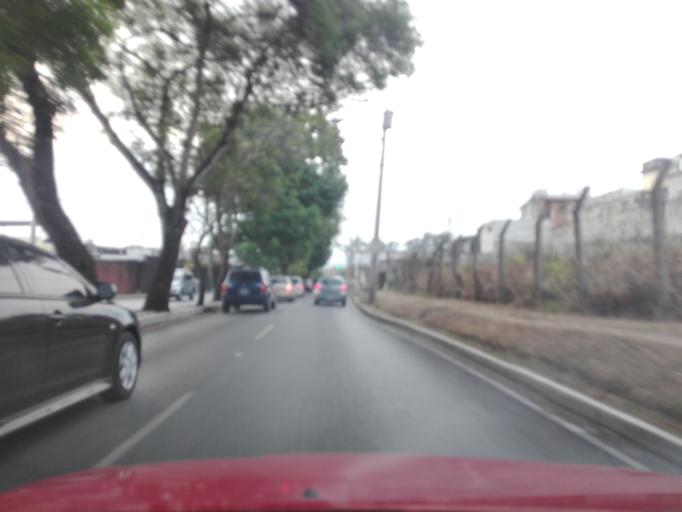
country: GT
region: Guatemala
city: Guatemala City
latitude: 14.6416
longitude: -90.5493
